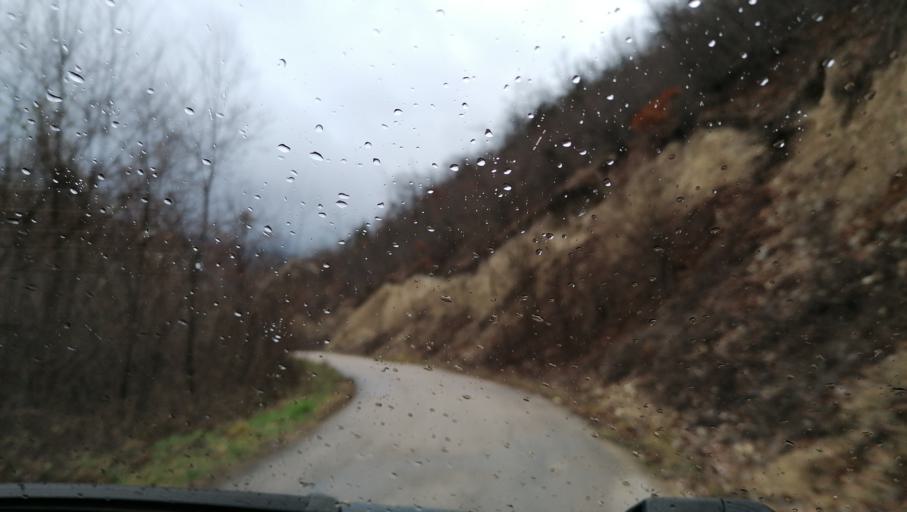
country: RS
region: Central Serbia
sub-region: Pirotski Okrug
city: Dimitrovgrad
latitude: 42.9808
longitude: 22.6487
